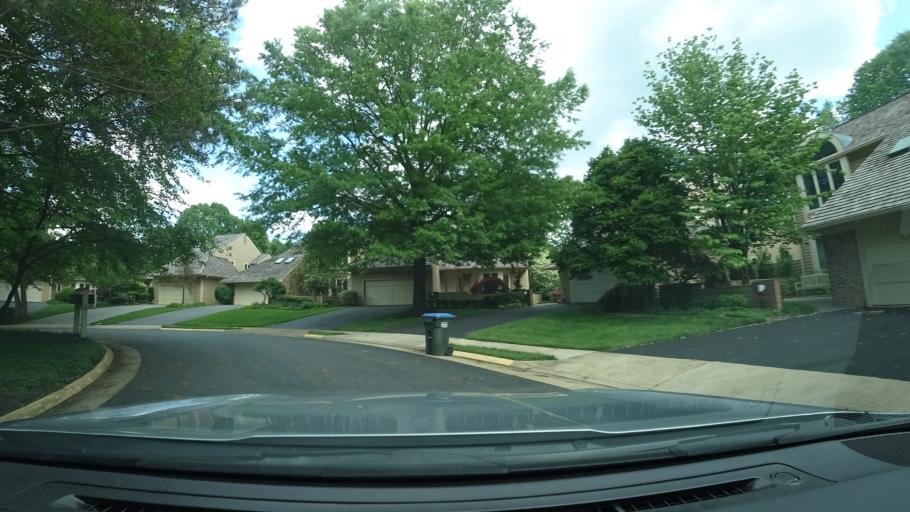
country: US
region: Virginia
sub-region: Fairfax County
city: Reston
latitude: 38.9764
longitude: -77.3412
